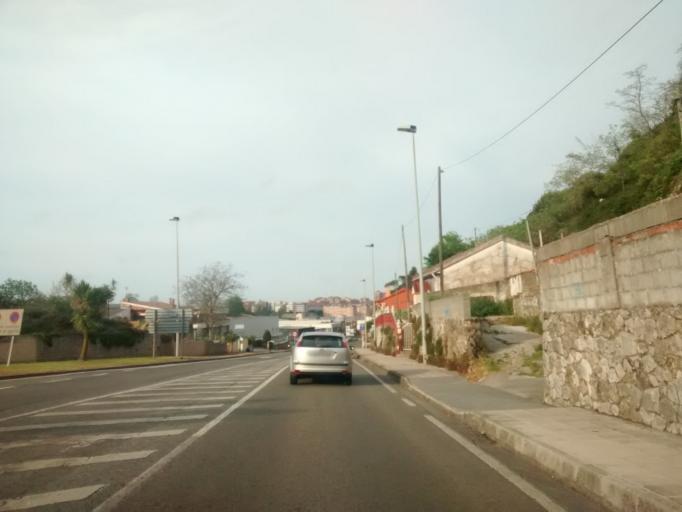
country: ES
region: Cantabria
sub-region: Provincia de Cantabria
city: Santa Cruz de Bezana
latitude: 43.4486
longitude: -3.8640
